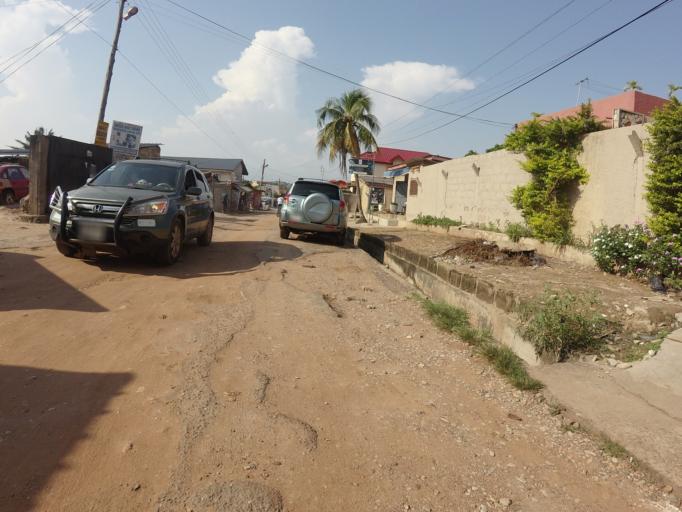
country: GH
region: Greater Accra
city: Dome
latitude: 5.6106
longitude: -0.2436
